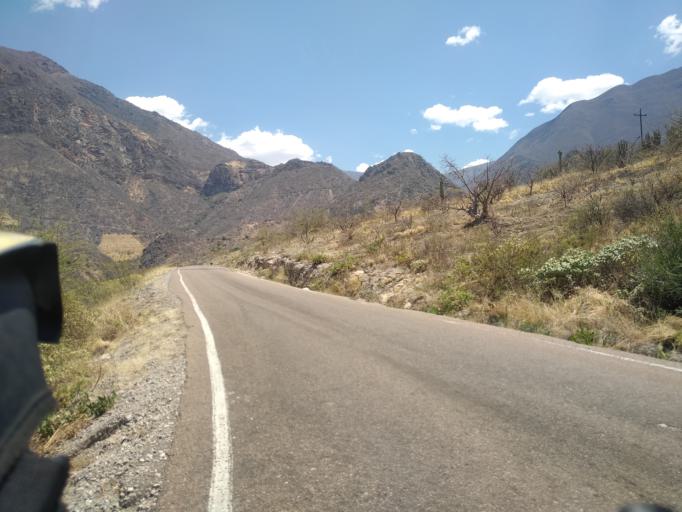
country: PE
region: Amazonas
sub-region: Provincia de Chachapoyas
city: Balsas
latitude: -6.8468
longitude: -78.0374
